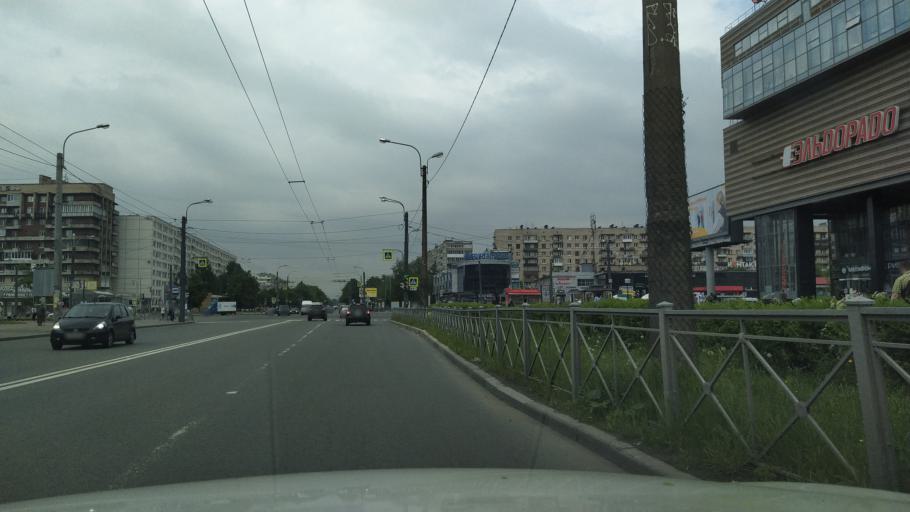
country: RU
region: St.-Petersburg
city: Kupchino
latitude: 59.8706
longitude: 30.3784
